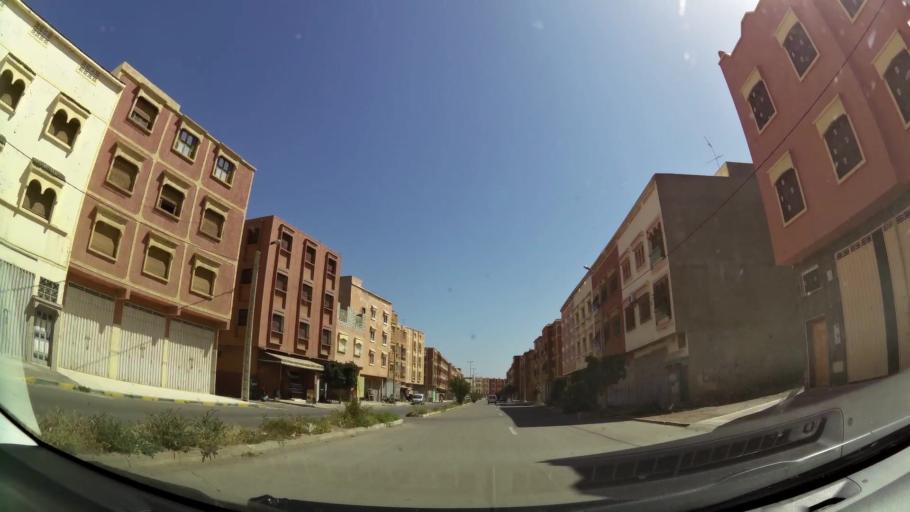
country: MA
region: Souss-Massa-Draa
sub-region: Inezgane-Ait Mellou
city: Inezgane
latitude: 30.3316
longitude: -9.5083
